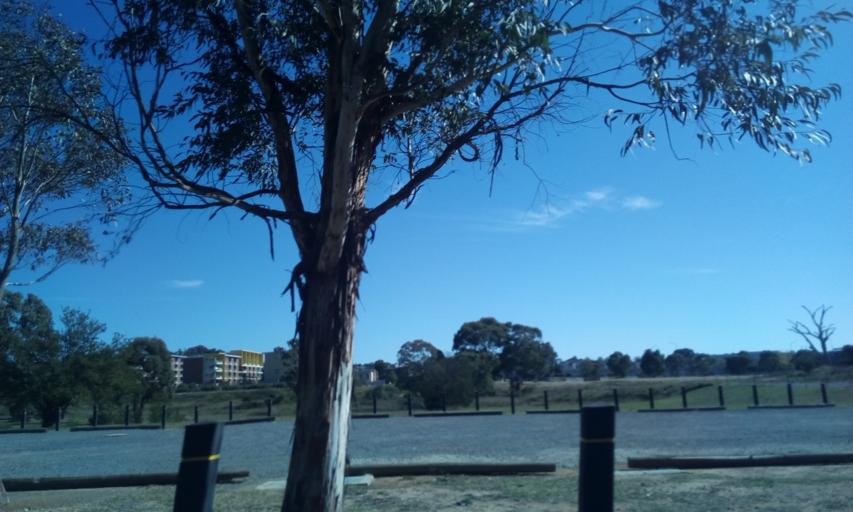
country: AU
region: Australian Capital Territory
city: Kaleen
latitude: -35.2437
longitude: 149.1034
